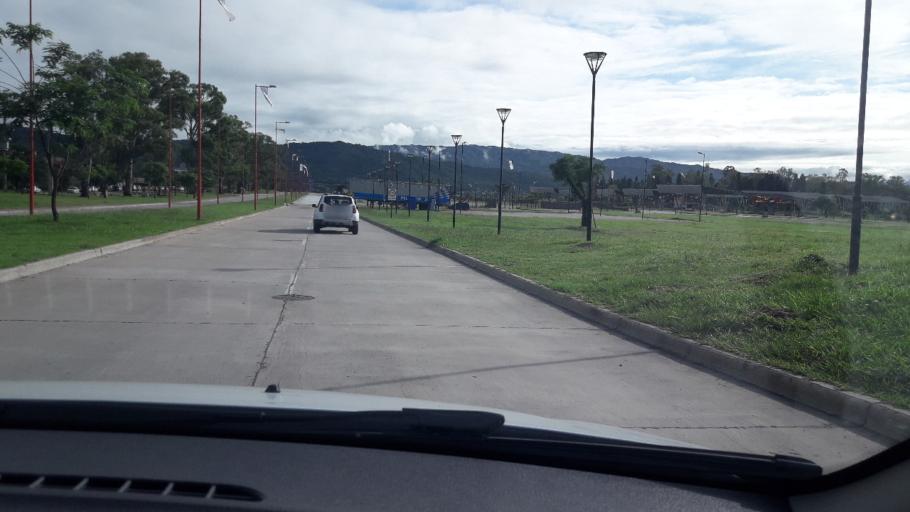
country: AR
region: Jujuy
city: San Salvador de Jujuy
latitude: -24.1844
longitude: -65.3328
